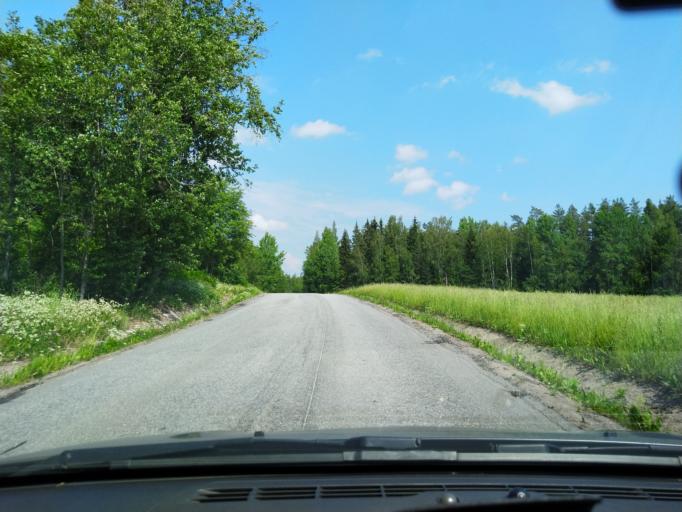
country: FI
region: Uusimaa
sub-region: Helsinki
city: Lohja
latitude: 60.3592
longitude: 24.0957
